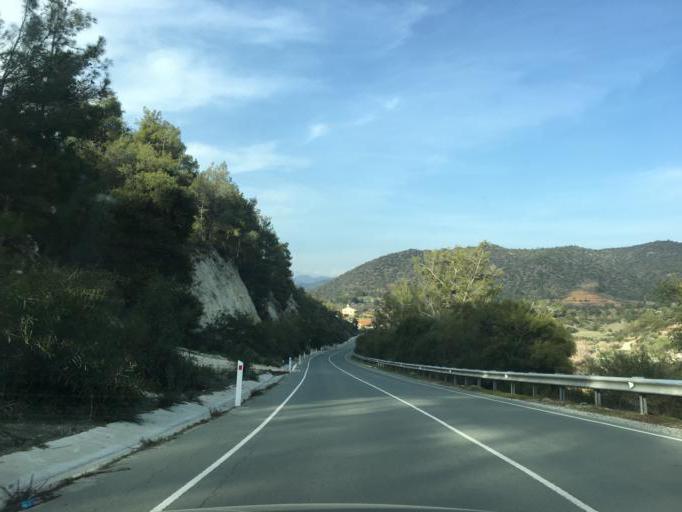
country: CY
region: Limassol
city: Pelendri
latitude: 34.8148
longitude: 32.9617
